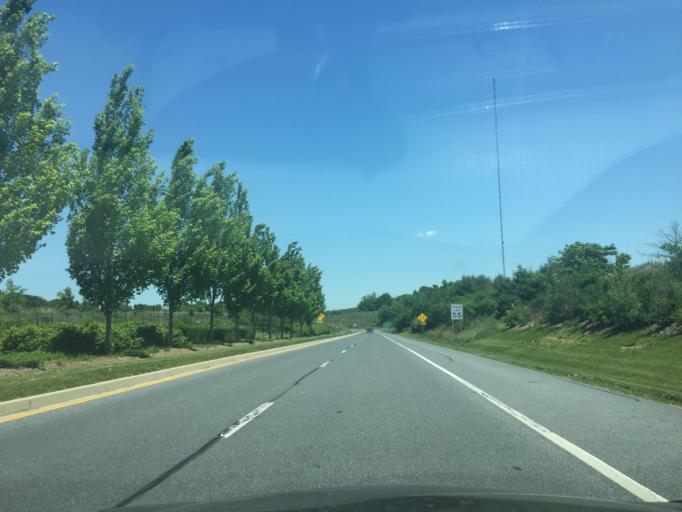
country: US
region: Maryland
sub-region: Carroll County
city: Hampstead
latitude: 39.6120
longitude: -76.8640
